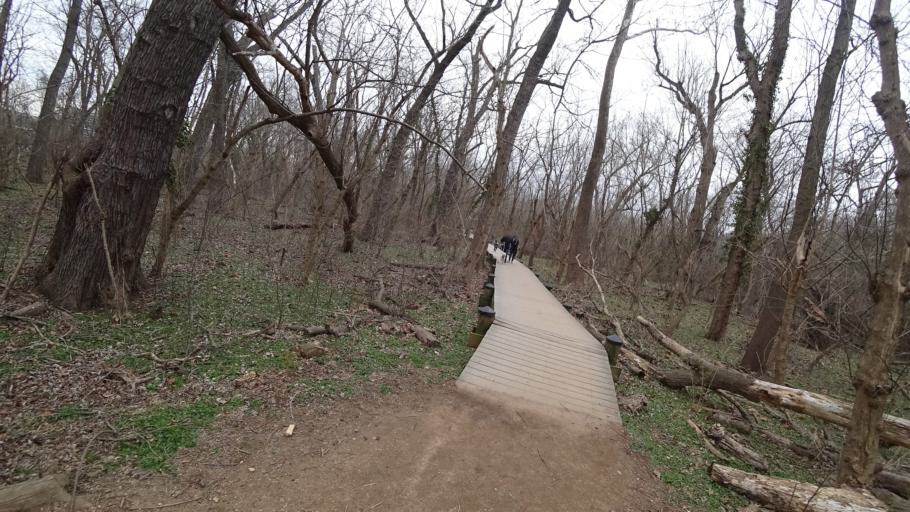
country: US
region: Washington, D.C.
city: Washington, D.C.
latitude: 38.8993
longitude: -77.0628
